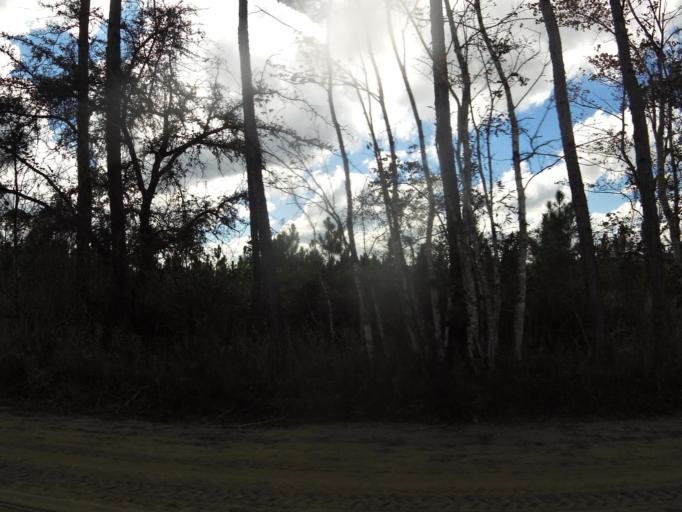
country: US
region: Florida
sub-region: Clay County
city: Green Cove Springs
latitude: 29.8369
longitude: -81.7717
